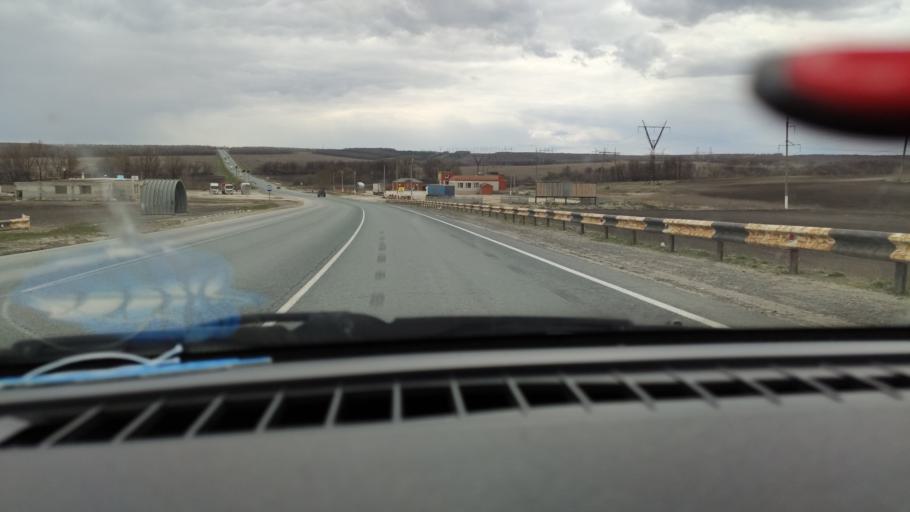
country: RU
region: Saratov
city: Sinodskoye
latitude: 51.9198
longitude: 46.5593
